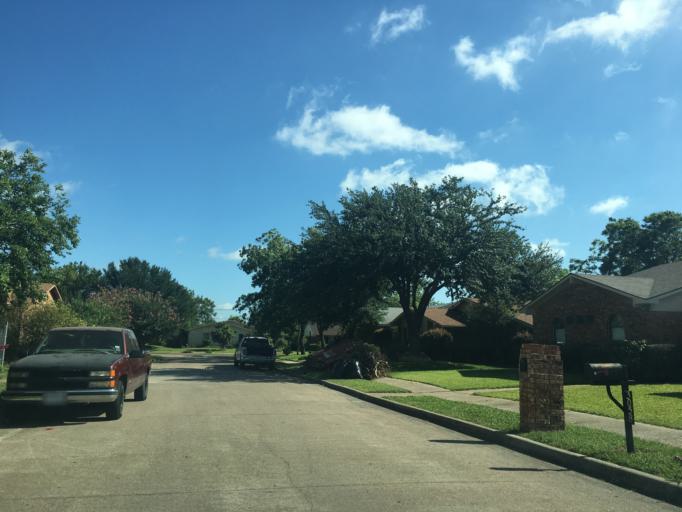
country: US
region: Texas
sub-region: Dallas County
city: Garland
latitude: 32.8515
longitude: -96.6601
